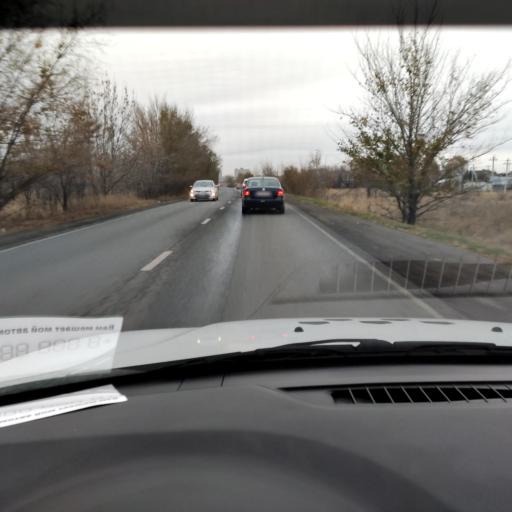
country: RU
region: Samara
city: Podstepki
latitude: 53.5159
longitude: 49.2363
